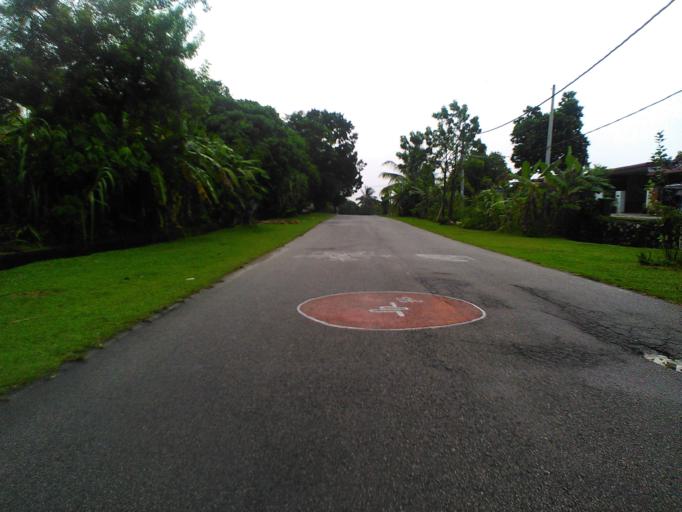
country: MY
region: Kedah
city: Kulim
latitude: 5.3646
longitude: 100.5710
